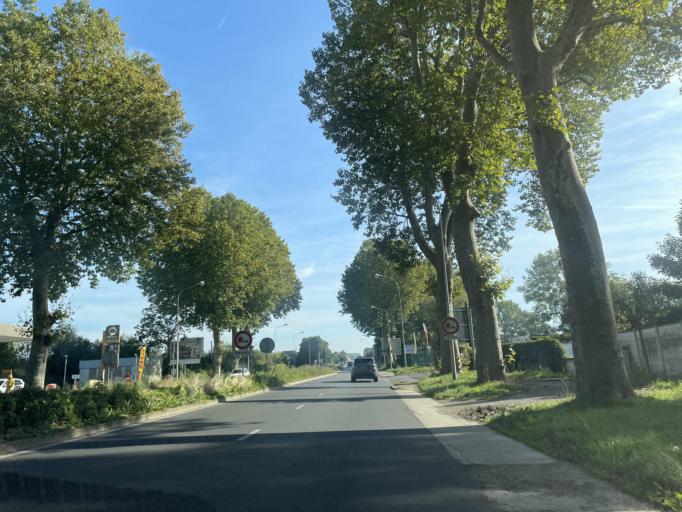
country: FR
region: Ile-de-France
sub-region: Departement de Seine-et-Marne
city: Trilport
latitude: 48.9575
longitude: 2.9399
